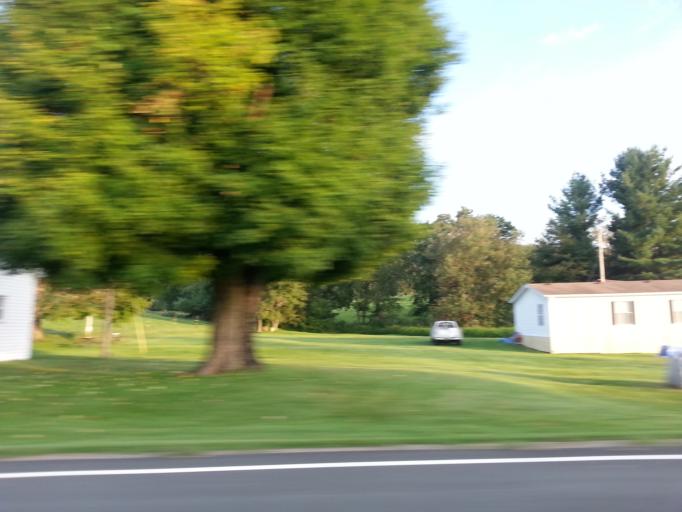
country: US
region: Tennessee
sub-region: Johnson County
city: Mountain City
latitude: 36.5291
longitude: -81.9085
